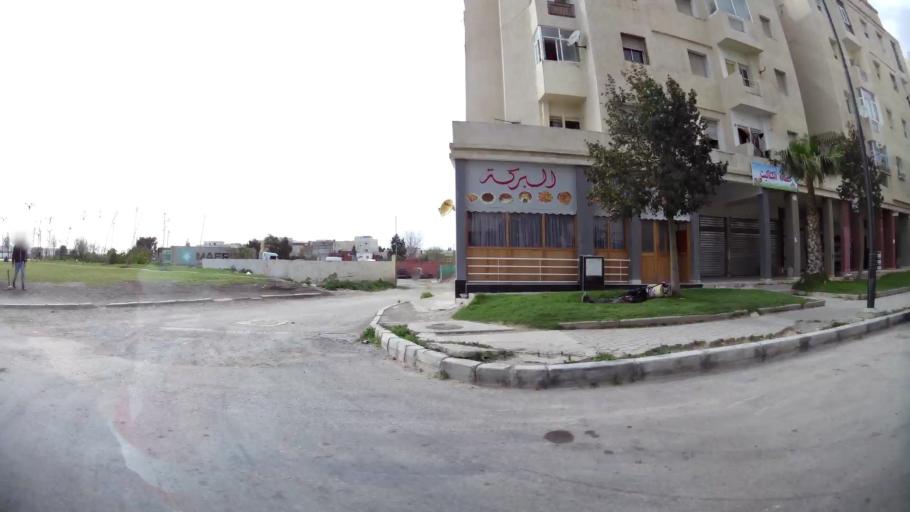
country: MA
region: Tanger-Tetouan
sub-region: Tanger-Assilah
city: Boukhalef
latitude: 35.7307
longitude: -5.8829
